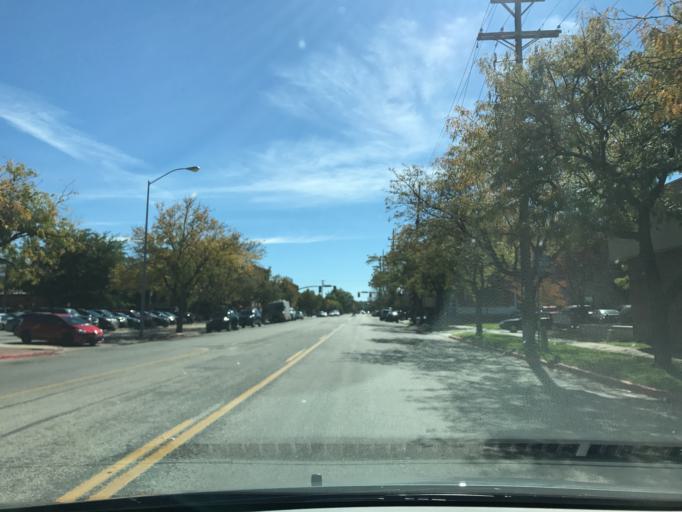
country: US
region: Utah
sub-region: Weber County
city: Ogden
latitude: 41.2220
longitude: -111.9760
